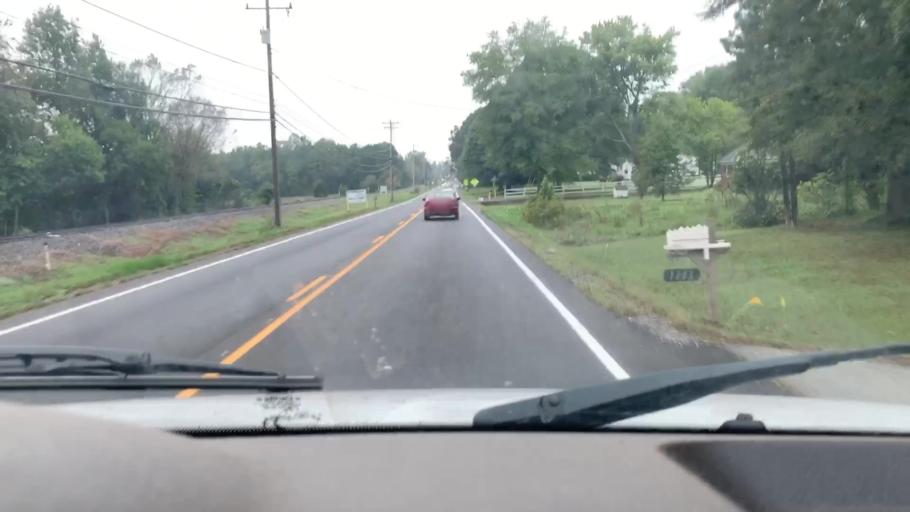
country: US
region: North Carolina
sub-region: Gaston County
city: Davidson
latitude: 35.5310
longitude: -80.8453
